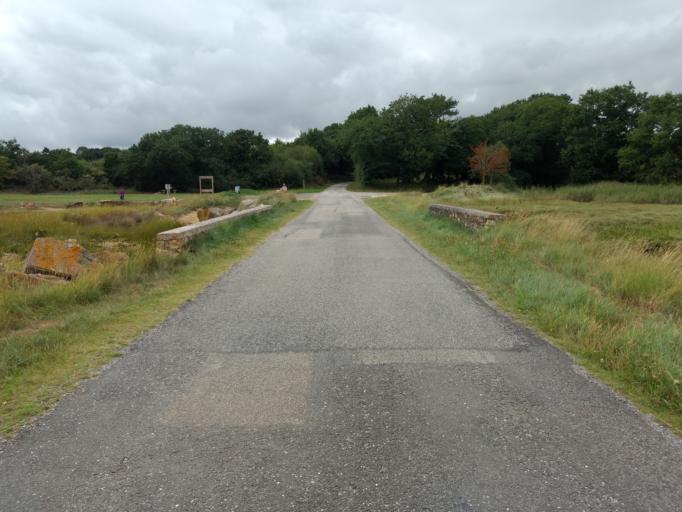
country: FR
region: Brittany
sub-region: Departement du Finistere
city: Loperhet
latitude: 48.3561
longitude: -4.2973
